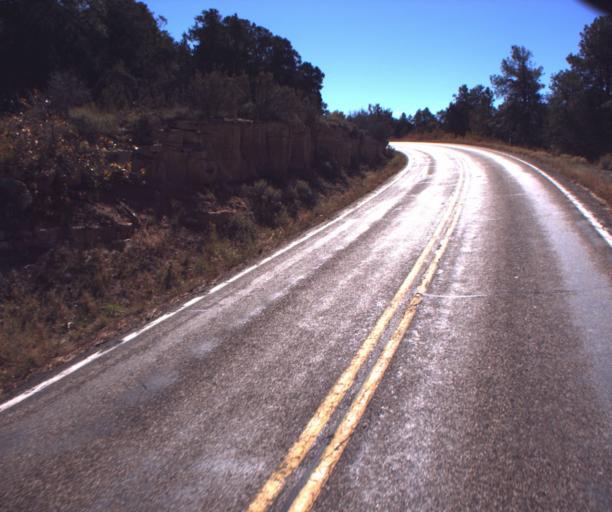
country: US
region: Arizona
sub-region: Coconino County
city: Fredonia
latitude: 36.7763
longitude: -112.2557
